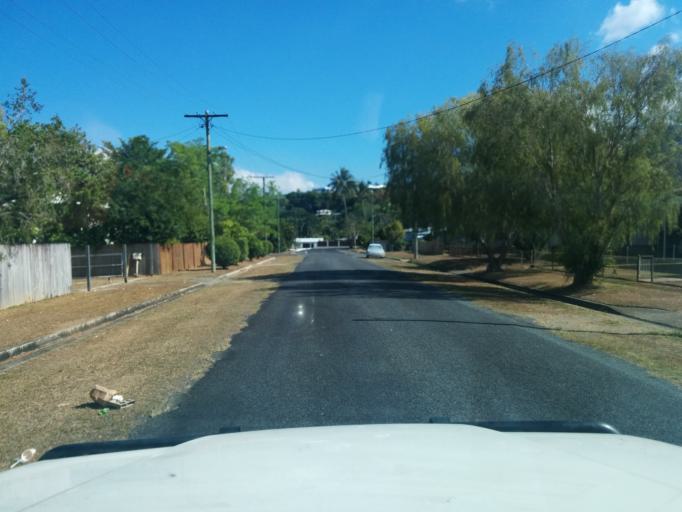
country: AU
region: Queensland
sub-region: Cairns
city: Woree
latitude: -16.9473
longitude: 145.7308
